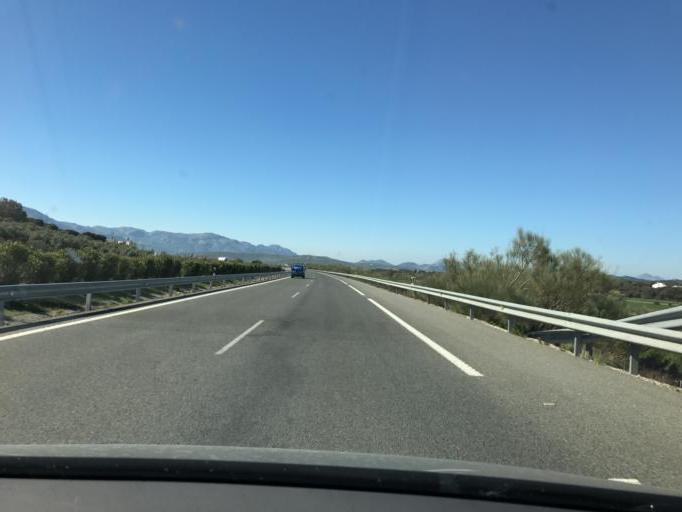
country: ES
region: Andalusia
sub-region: Provincia de Malaga
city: Archidona
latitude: 37.1055
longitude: -4.3119
